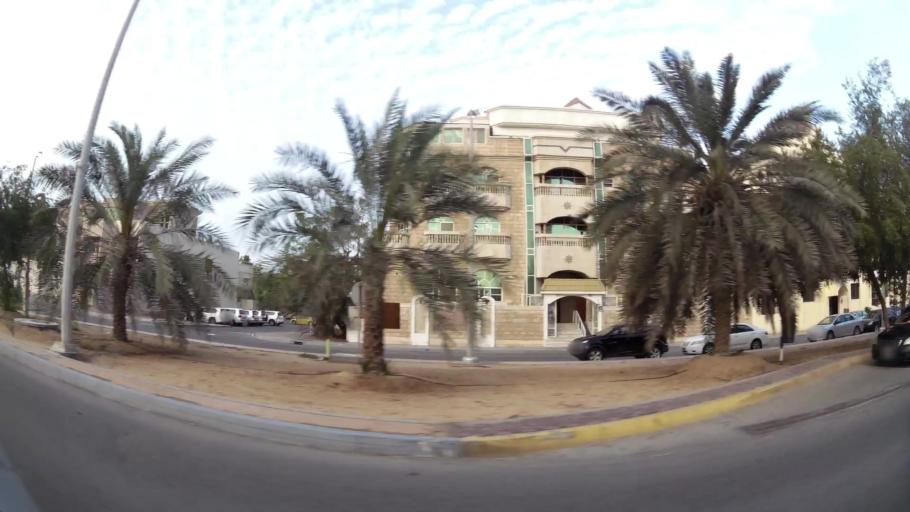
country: AE
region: Abu Dhabi
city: Abu Dhabi
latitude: 24.4585
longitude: 54.3590
